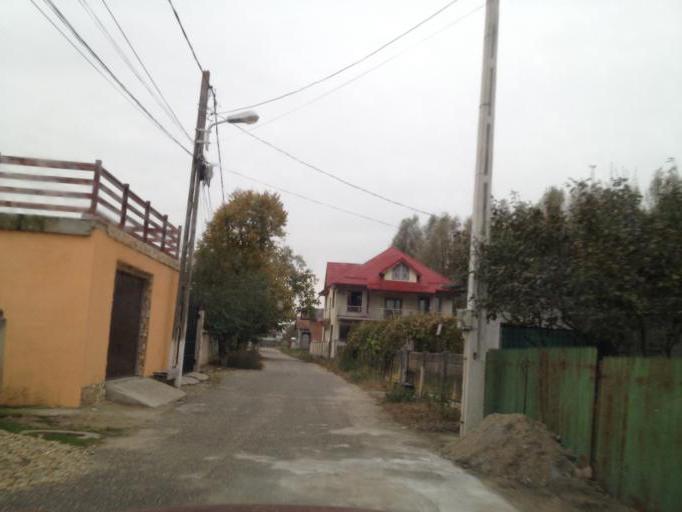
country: RO
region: Dolj
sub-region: Municipiul Craiova
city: Mofleni
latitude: 44.2988
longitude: 23.7567
